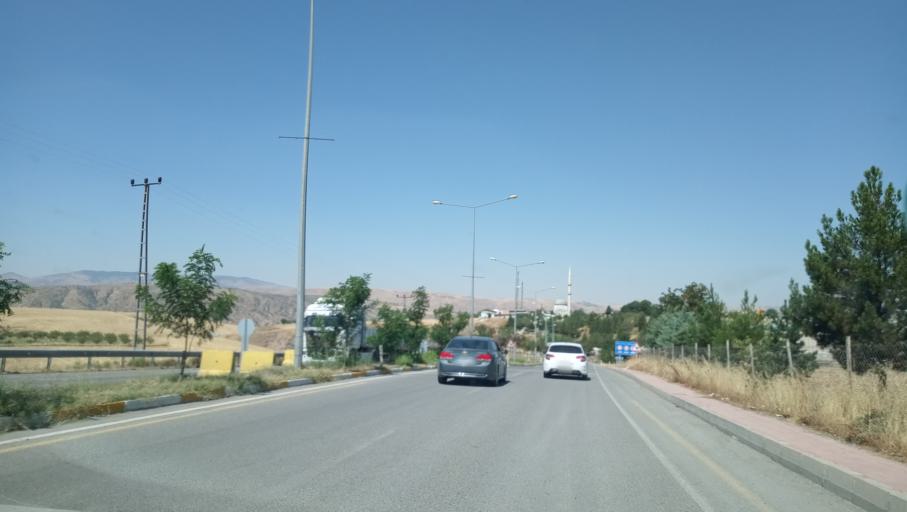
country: TR
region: Siirt
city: Civankan
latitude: 37.9515
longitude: 41.8829
